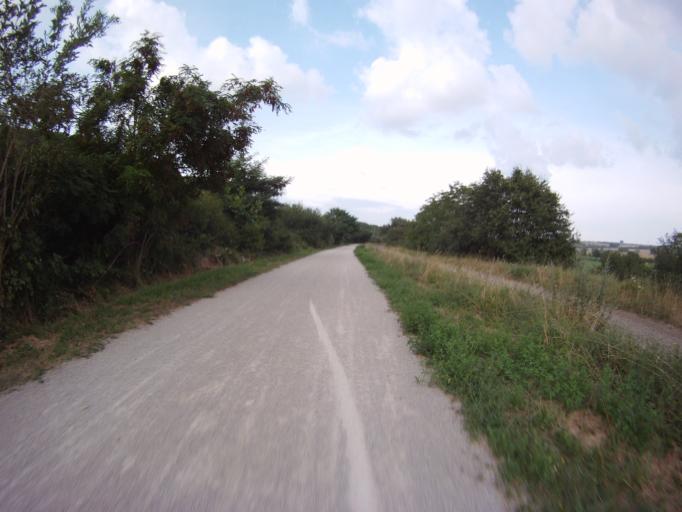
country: FR
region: Lorraine
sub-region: Departement de la Moselle
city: Courcelles-Chaussy
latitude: 49.0912
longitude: 6.3625
